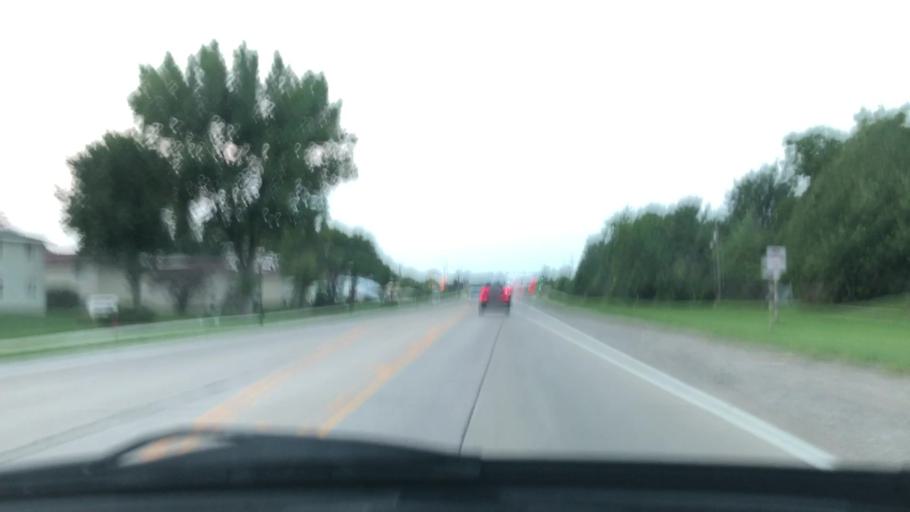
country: US
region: Iowa
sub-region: Johnson County
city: North Liberty
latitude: 41.7417
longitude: -91.6076
